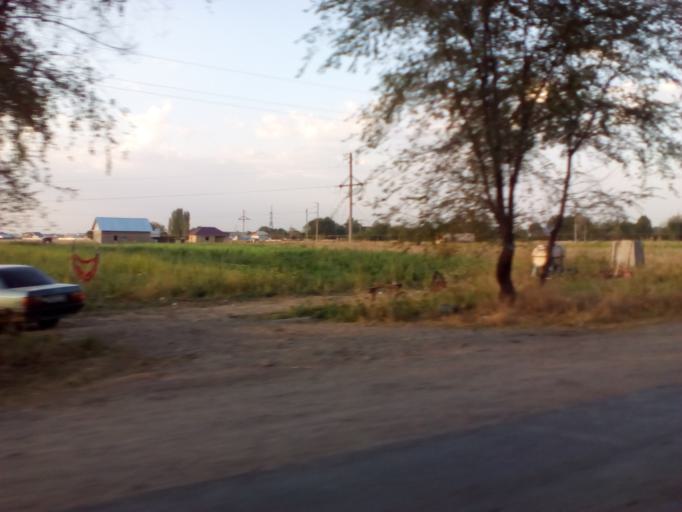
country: KZ
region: Almaty Oblysy
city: Burunday
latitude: 43.1662
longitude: 76.3964
